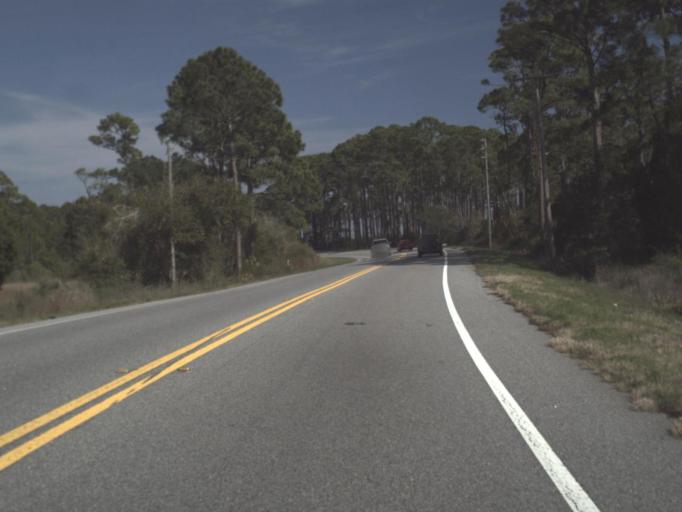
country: US
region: Florida
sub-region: Franklin County
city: Carrabelle
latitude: 29.7931
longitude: -84.7541
